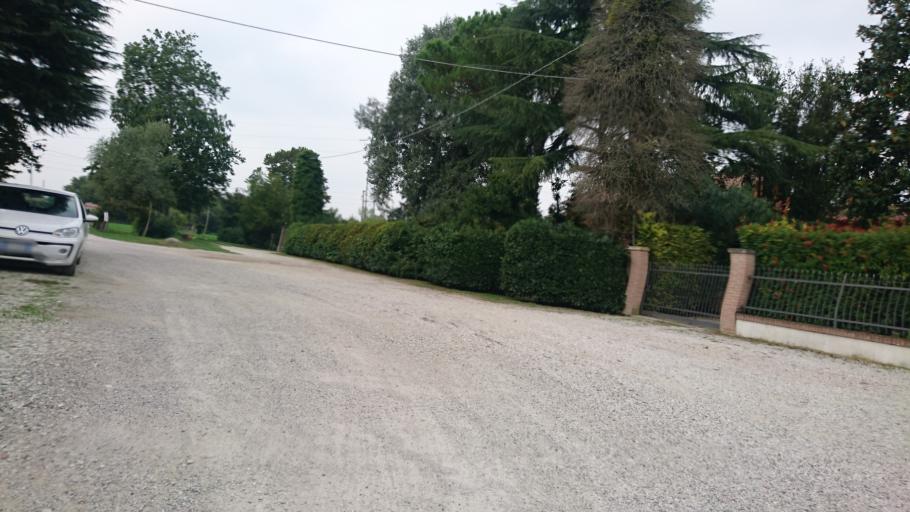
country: IT
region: Veneto
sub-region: Provincia di Padova
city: Tencarola
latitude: 45.3974
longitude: 11.8180
